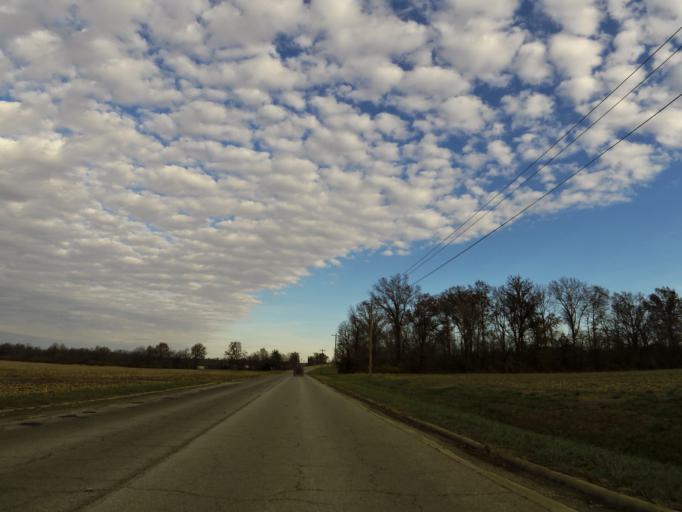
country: US
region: Illinois
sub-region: Jefferson County
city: Mount Vernon
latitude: 38.3380
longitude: -88.9699
